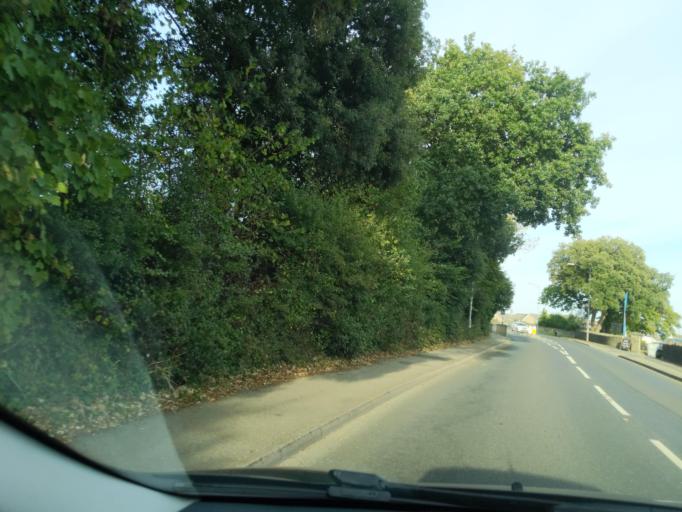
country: GB
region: England
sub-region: Cornwall
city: Torpoint
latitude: 50.3761
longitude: -4.2085
